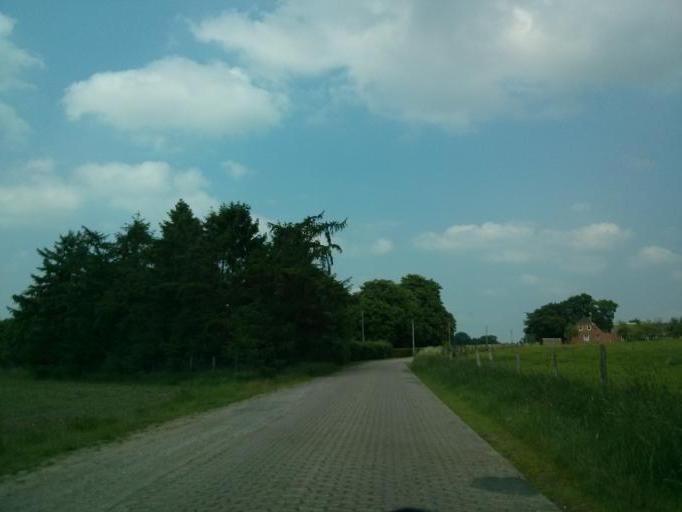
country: DE
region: Lower Saxony
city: Schiffdorf
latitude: 53.5020
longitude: 8.6916
